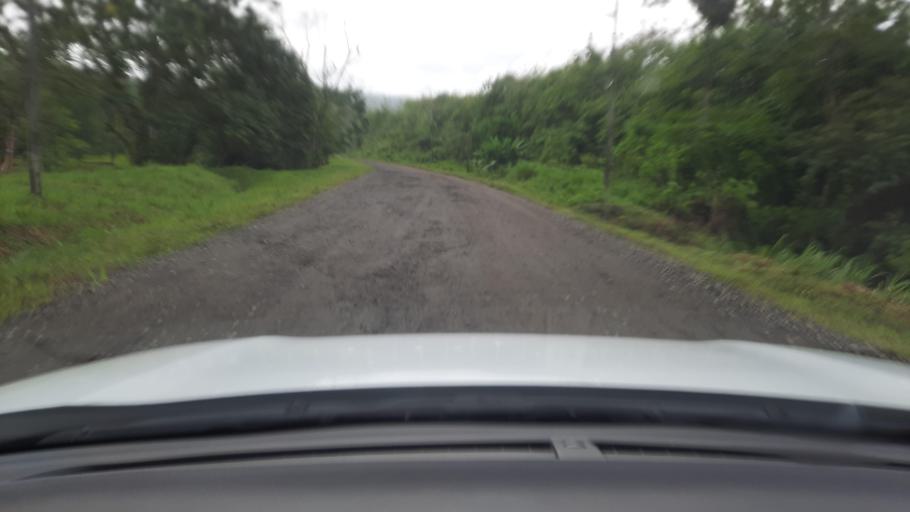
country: CR
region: Alajuela
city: San Jose
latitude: 11.0003
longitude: -85.2880
